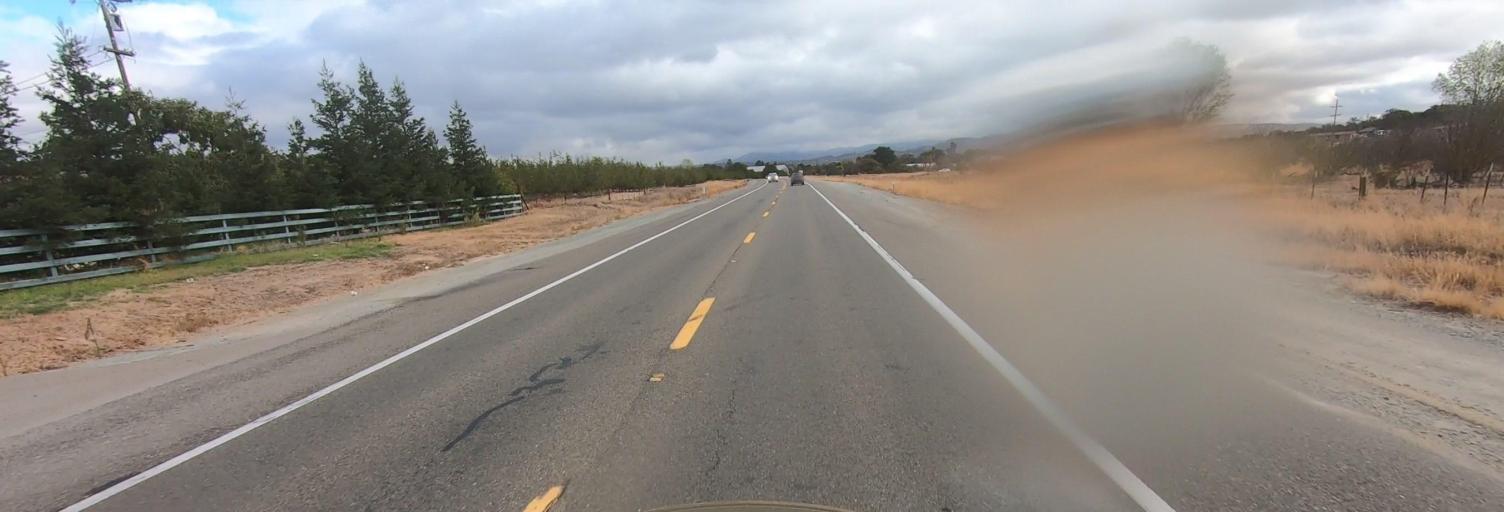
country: US
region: California
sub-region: Calaveras County
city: Rancho Calaveras
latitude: 38.0995
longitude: -120.9346
